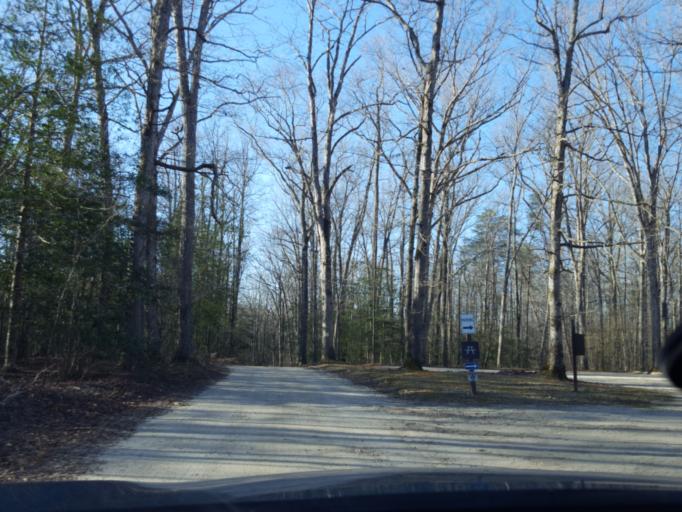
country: US
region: Maryland
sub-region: Prince George's County
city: Baden
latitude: 38.6435
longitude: -76.8175
